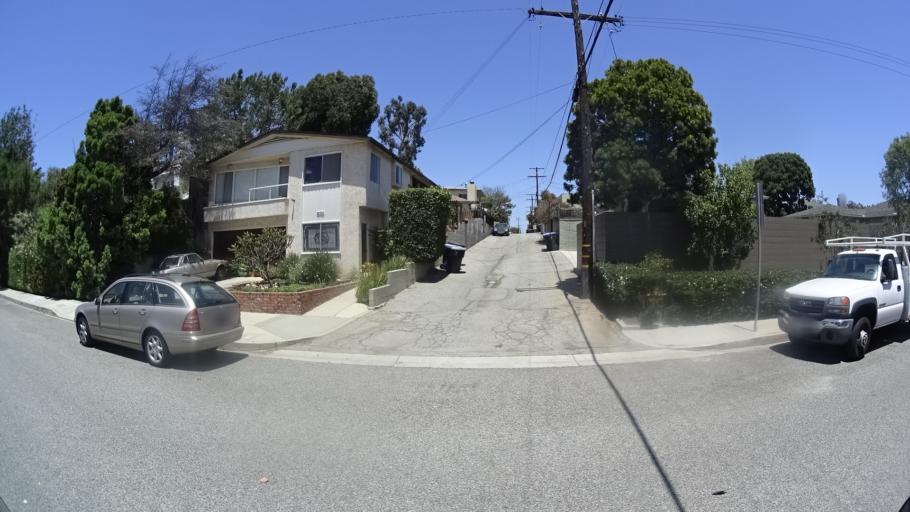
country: US
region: California
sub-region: Los Angeles County
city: Santa Monica
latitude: 34.0084
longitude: -118.4707
